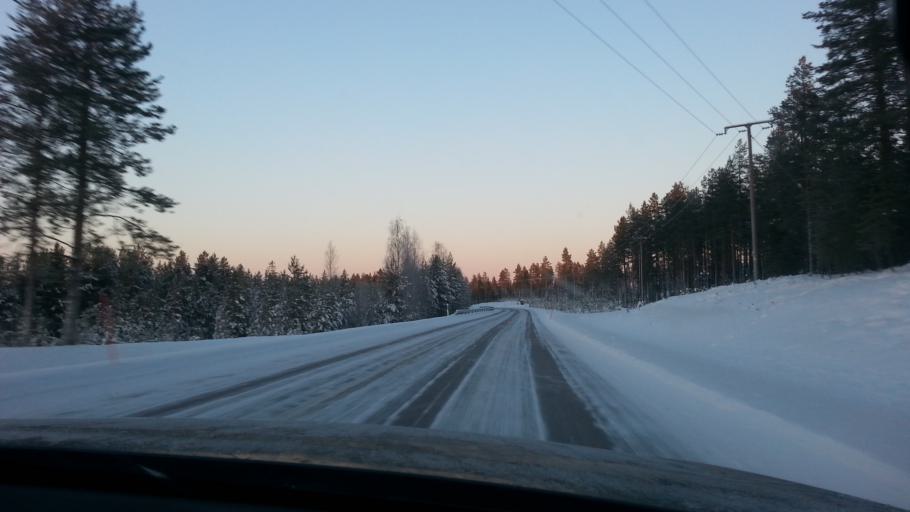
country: FI
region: Lapland
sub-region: Rovaniemi
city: Rovaniemi
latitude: 66.7839
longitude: 25.4441
